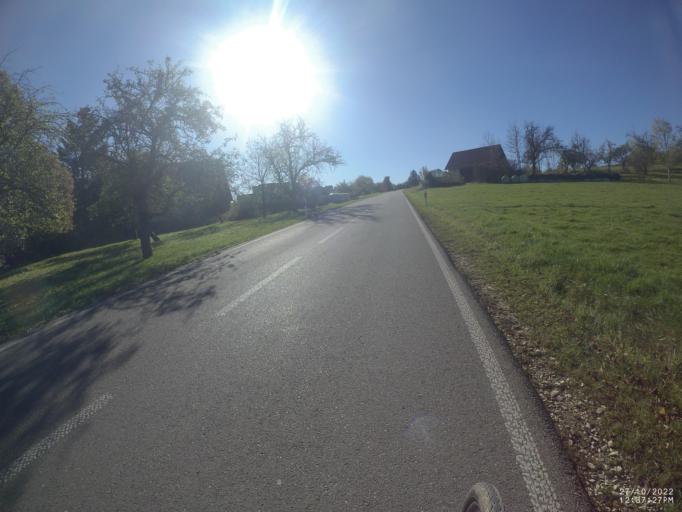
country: DE
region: Baden-Wuerttemberg
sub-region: Regierungsbezirk Stuttgart
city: Hohenstadt
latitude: 48.5550
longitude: 9.6817
